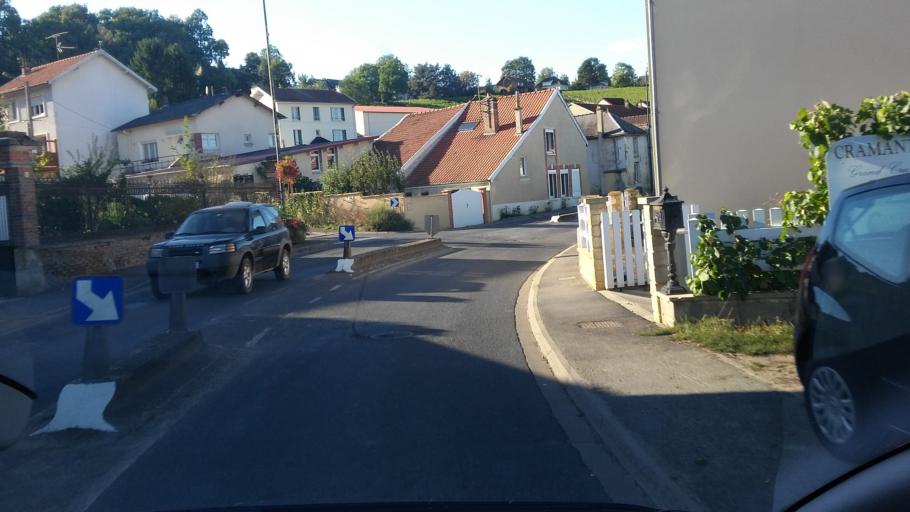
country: FR
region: Champagne-Ardenne
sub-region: Departement de la Marne
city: Avize
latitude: 48.9819
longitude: 3.9929
